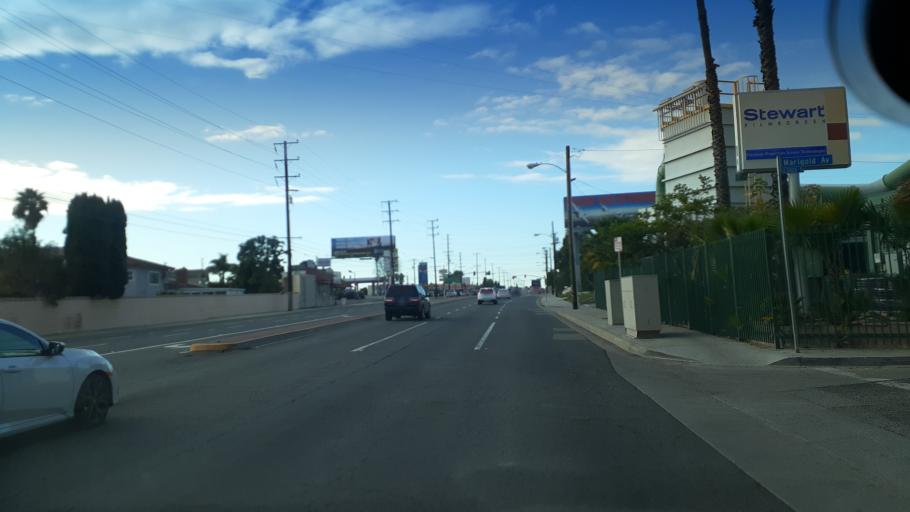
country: US
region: California
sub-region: Los Angeles County
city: West Carson
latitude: 33.8124
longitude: -118.2959
